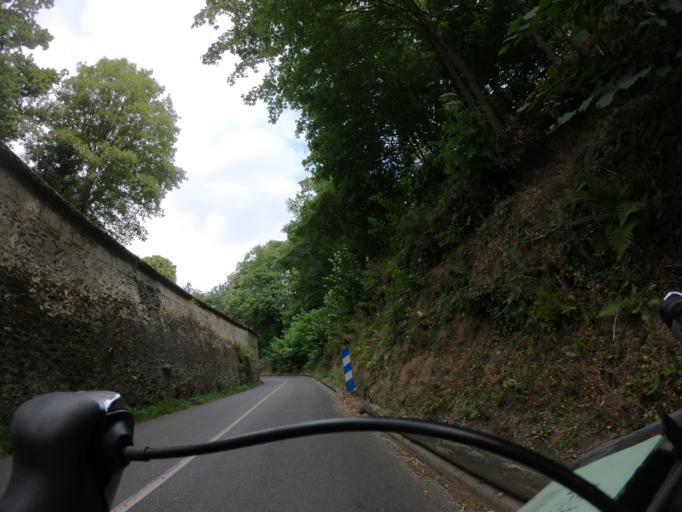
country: FR
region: Ile-de-France
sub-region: Departement de l'Essonne
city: Igny
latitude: 48.7469
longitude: 2.2321
